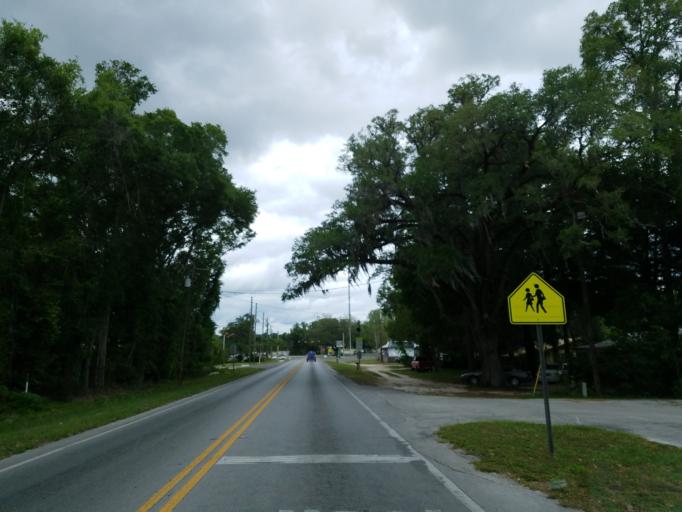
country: US
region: Florida
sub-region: Marion County
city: Ocala
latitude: 29.2867
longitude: -82.1116
